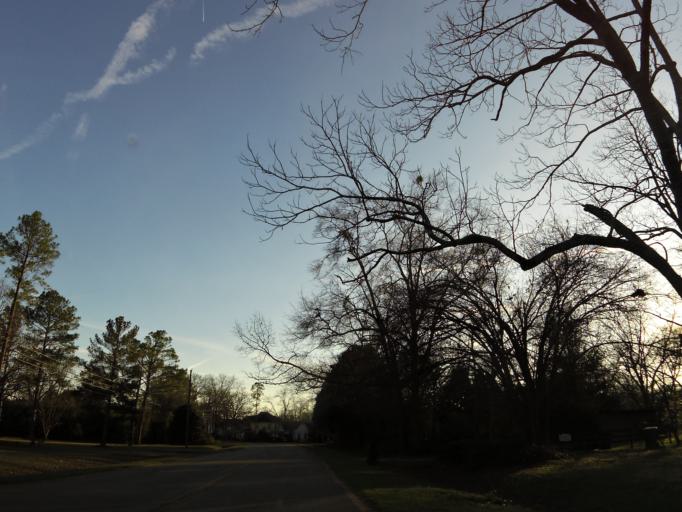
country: US
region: Georgia
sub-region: Webster County
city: Preston
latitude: 32.0394
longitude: -84.3934
